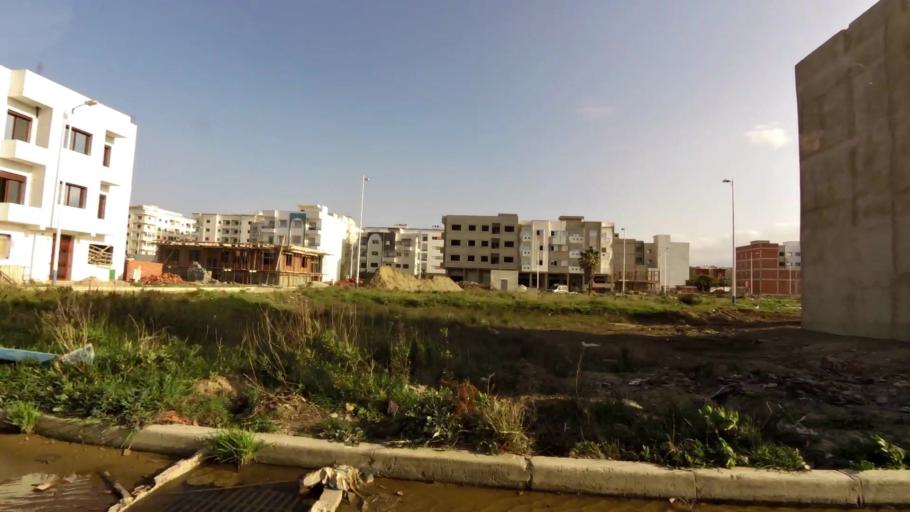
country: MA
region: Tanger-Tetouan
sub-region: Tetouan
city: Martil
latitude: 35.6306
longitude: -5.2769
